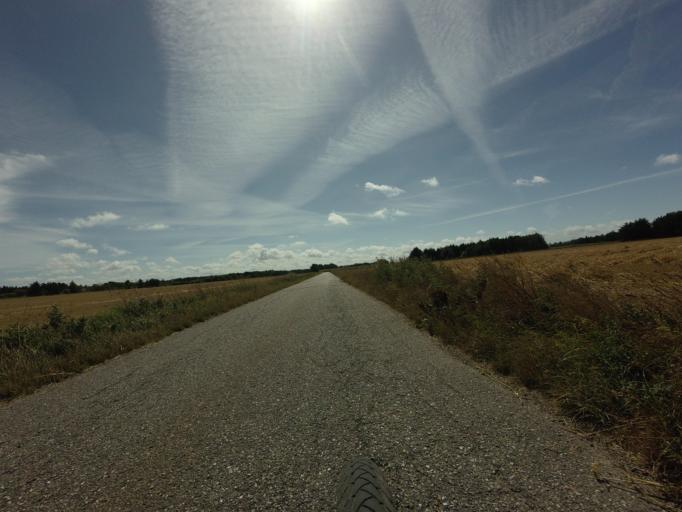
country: DK
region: North Denmark
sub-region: Hjorring Kommune
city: Vra
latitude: 57.3832
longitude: 9.7836
